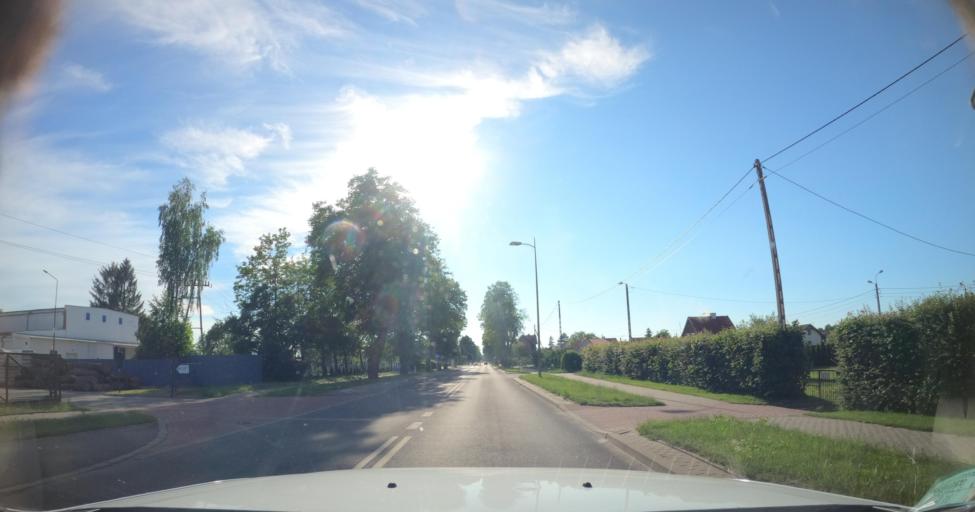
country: PL
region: Warmian-Masurian Voivodeship
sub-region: Powiat elblaski
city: Paslek
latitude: 54.0722
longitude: 19.6520
